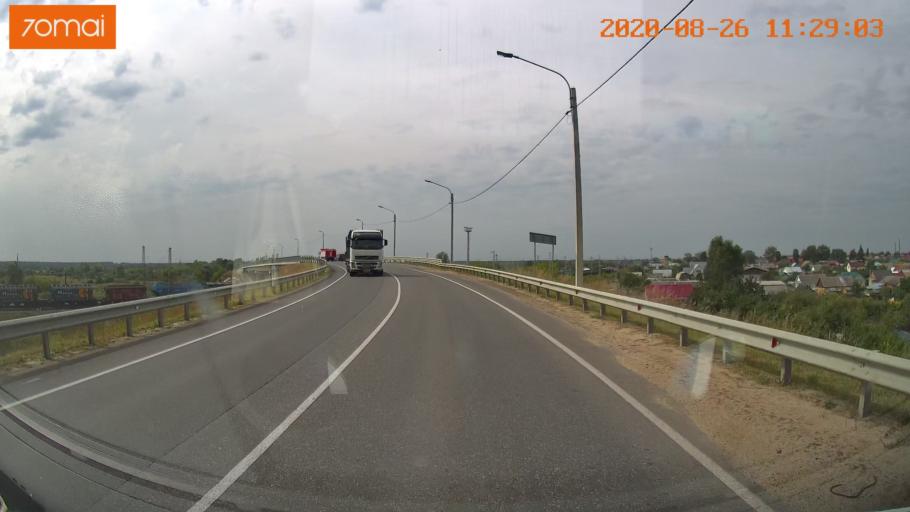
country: RU
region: Rjazan
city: Shilovo
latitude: 54.3230
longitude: 40.9021
